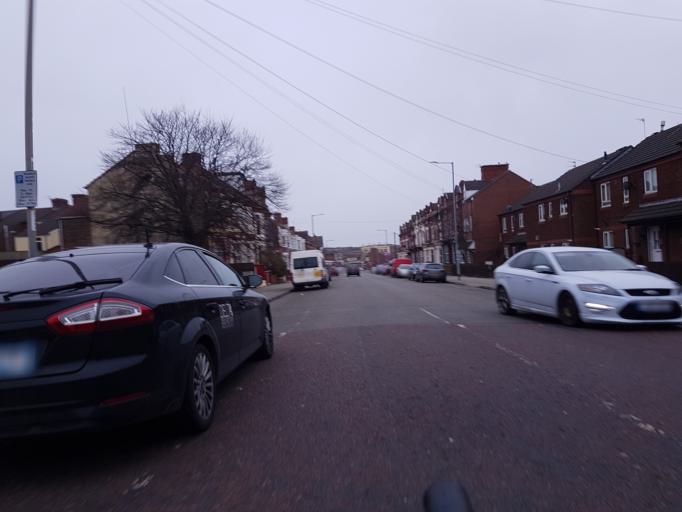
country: GB
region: England
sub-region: Liverpool
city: Liverpool
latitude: 53.4413
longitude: -2.9738
